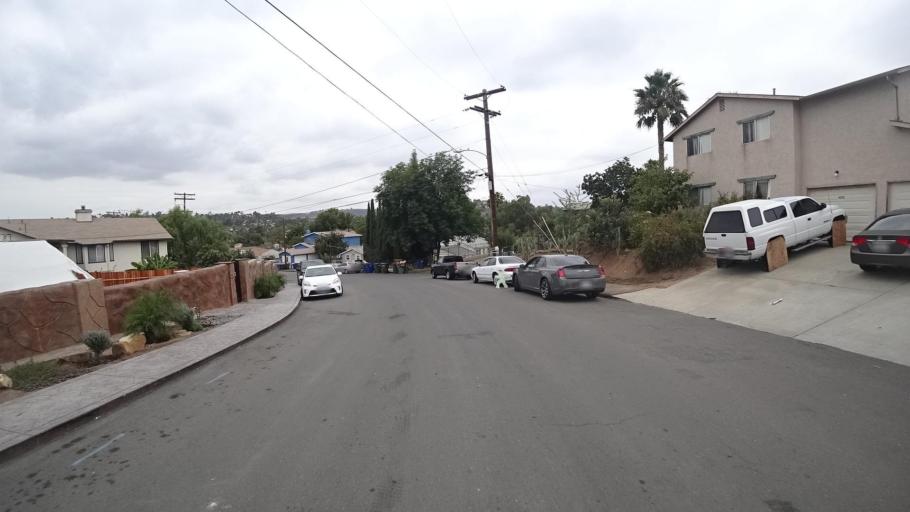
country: US
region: California
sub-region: San Diego County
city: Spring Valley
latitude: 32.7344
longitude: -117.0042
